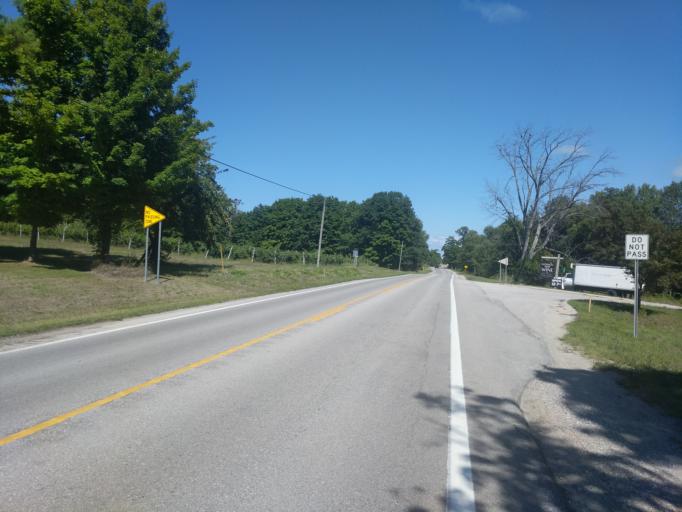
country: US
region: Michigan
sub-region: Leelanau County
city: Leland
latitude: 45.0089
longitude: -85.6192
